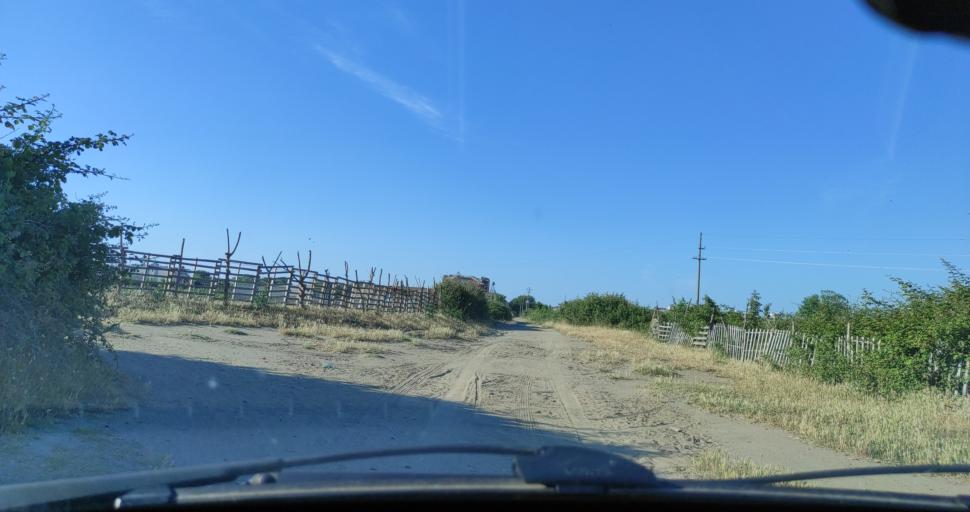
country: AL
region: Shkoder
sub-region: Rrethi i Shkodres
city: Velipoje
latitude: 41.8724
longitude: 19.4259
